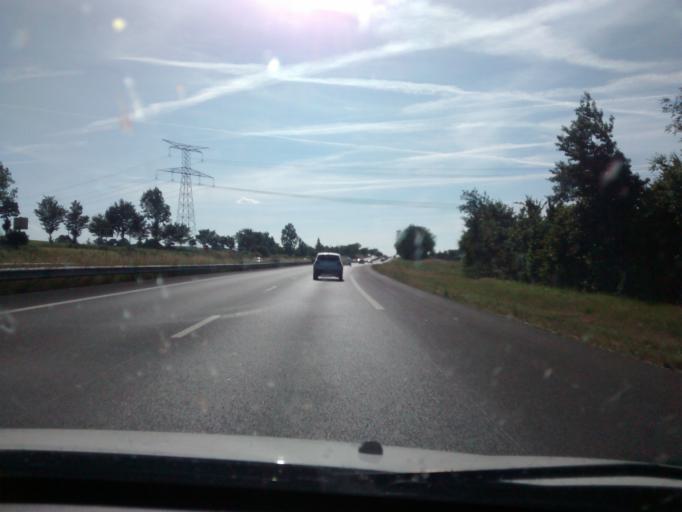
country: FR
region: Brittany
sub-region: Departement d'Ille-et-Vilaine
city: Servon-sur-Vilaine
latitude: 48.1016
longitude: -1.4384
